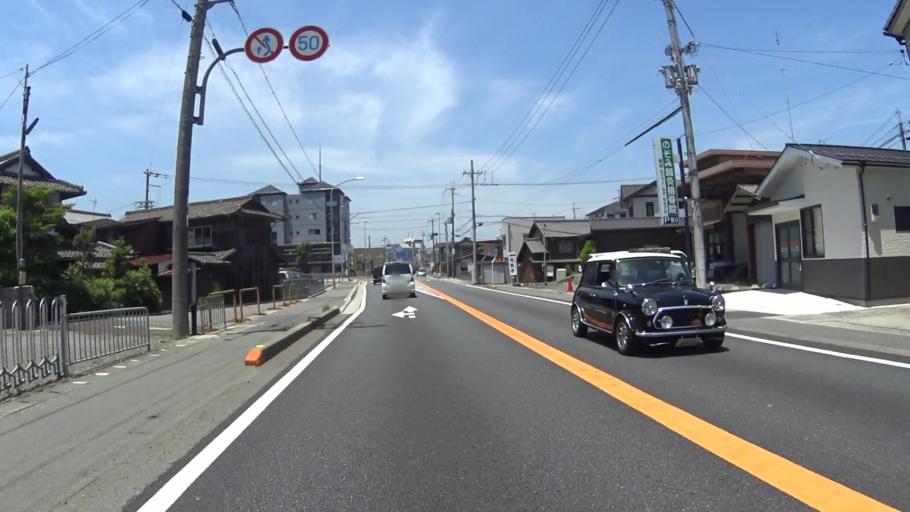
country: JP
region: Kyoto
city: Kameoka
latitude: 35.0681
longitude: 135.5354
